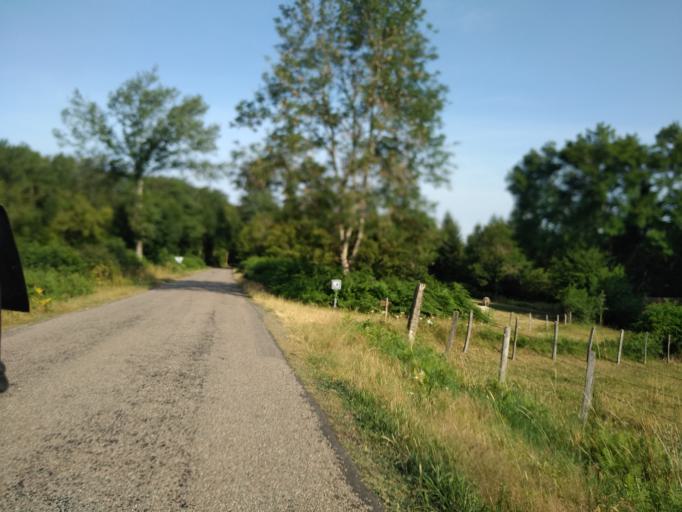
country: FR
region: Rhone-Alpes
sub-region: Departement de la Loire
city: Saint-Nizier-sous-Charlieu
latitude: 46.2403
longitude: 4.1260
